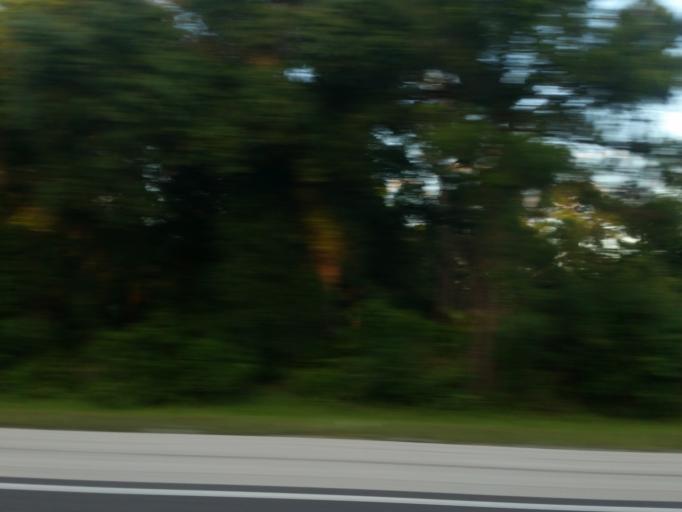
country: US
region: Florida
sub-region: Sarasota County
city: Bee Ridge
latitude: 27.2440
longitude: -82.4505
